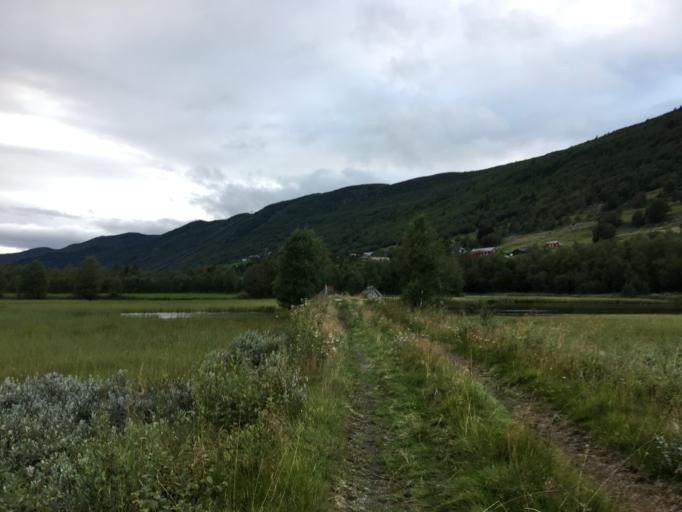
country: NO
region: Buskerud
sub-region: Hol
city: Hol
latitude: 60.6173
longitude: 8.2253
